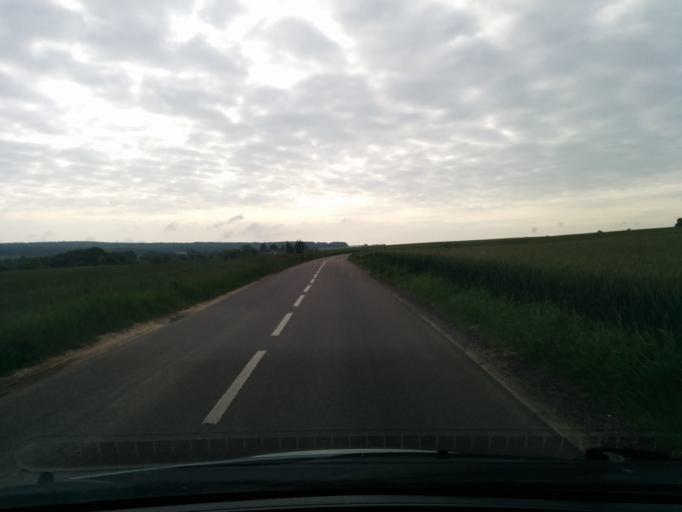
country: FR
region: Haute-Normandie
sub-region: Departement de l'Eure
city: Gasny
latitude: 49.0871
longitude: 1.6631
